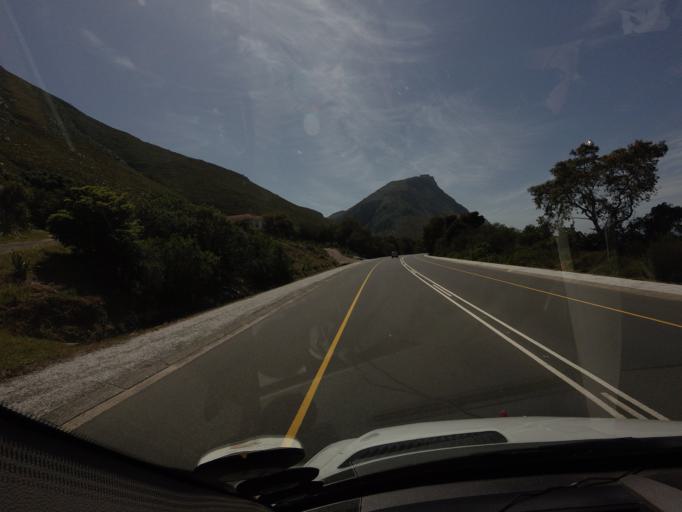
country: ZA
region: Western Cape
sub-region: Overberg District Municipality
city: Grabouw
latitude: -34.3513
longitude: 18.9169
